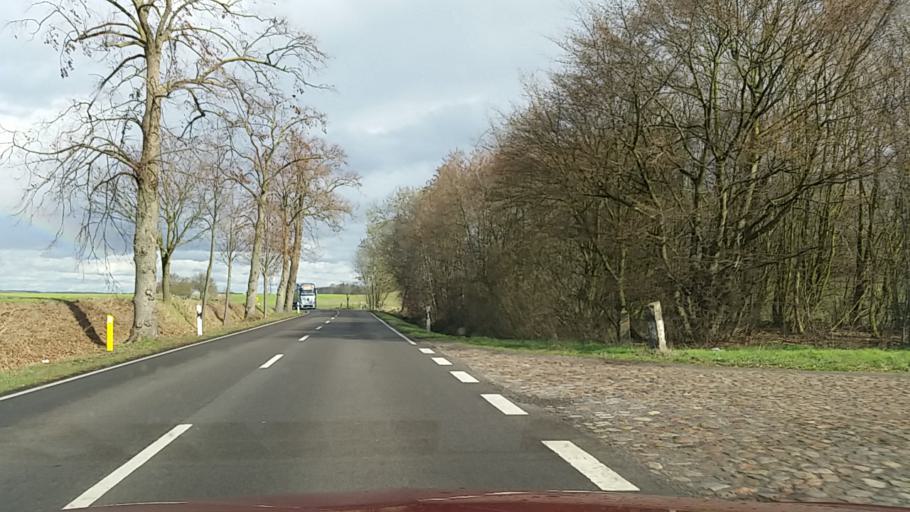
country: DE
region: Saxony-Anhalt
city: Rohrberg
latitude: 52.7349
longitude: 11.0586
